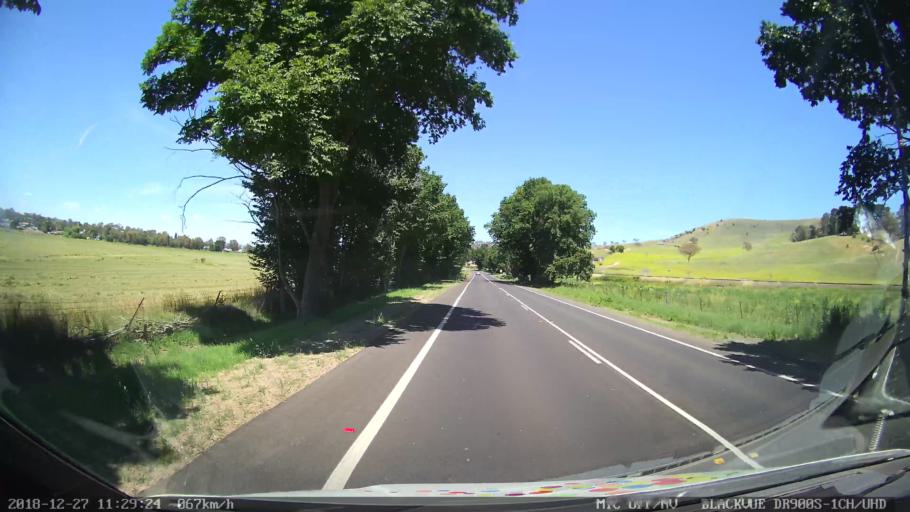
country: AU
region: New South Wales
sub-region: Bathurst Regional
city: Perthville
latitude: -33.4827
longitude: 149.5527
